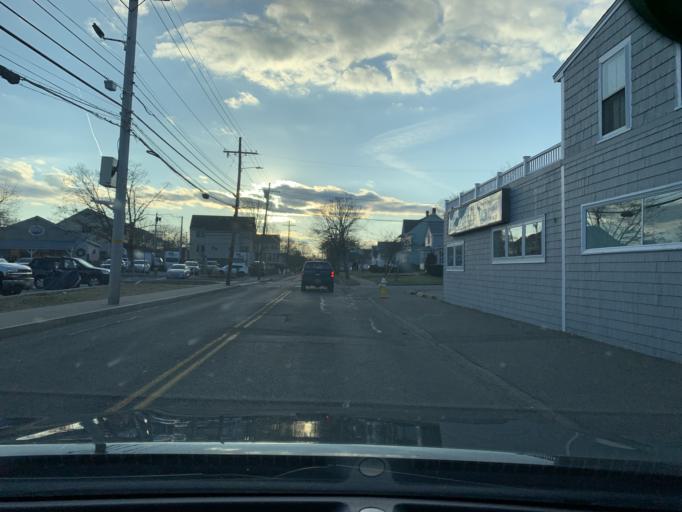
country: US
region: Massachusetts
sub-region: Essex County
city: Danvers
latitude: 42.5672
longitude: -70.9399
